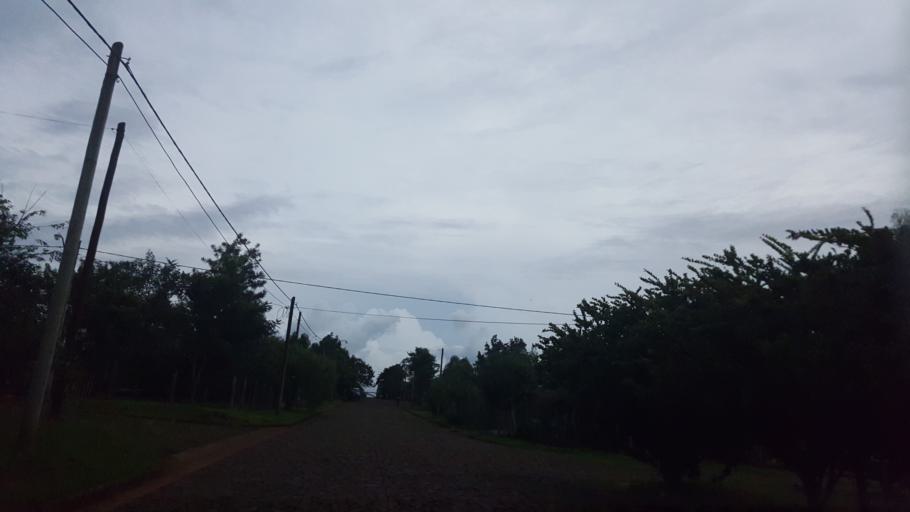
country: AR
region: Misiones
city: Capiovi
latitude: -26.9263
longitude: -55.0514
